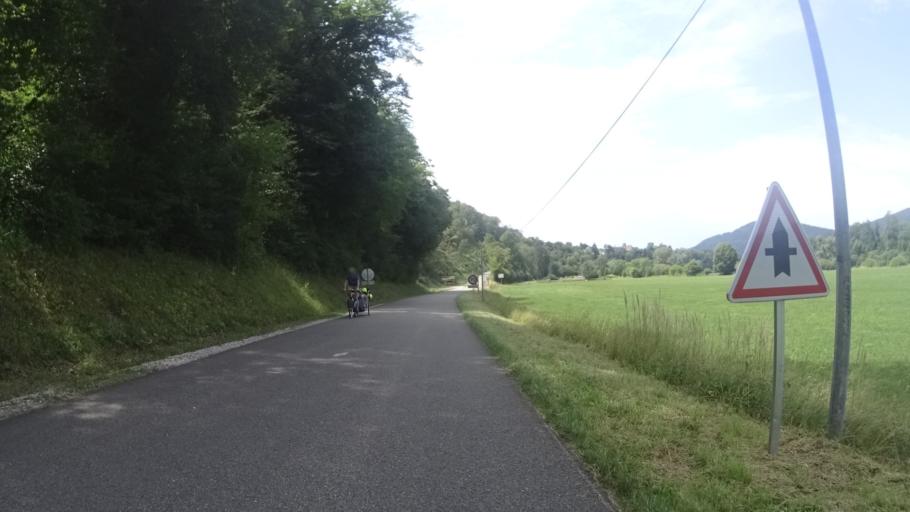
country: FR
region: Franche-Comte
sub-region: Departement du Doubs
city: Clerval
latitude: 47.3689
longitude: 6.4930
